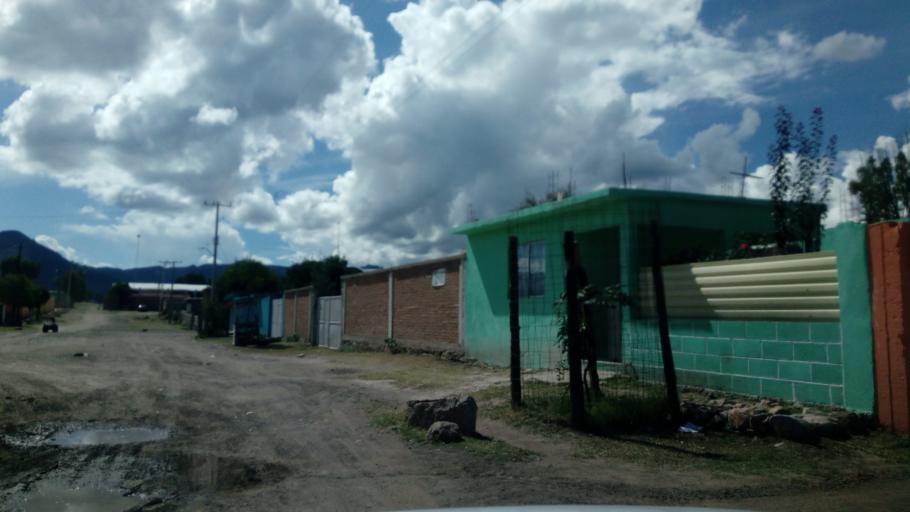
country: MX
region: Durango
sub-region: Durango
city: Jose Refugio Salcido
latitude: 23.7927
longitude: -104.4868
